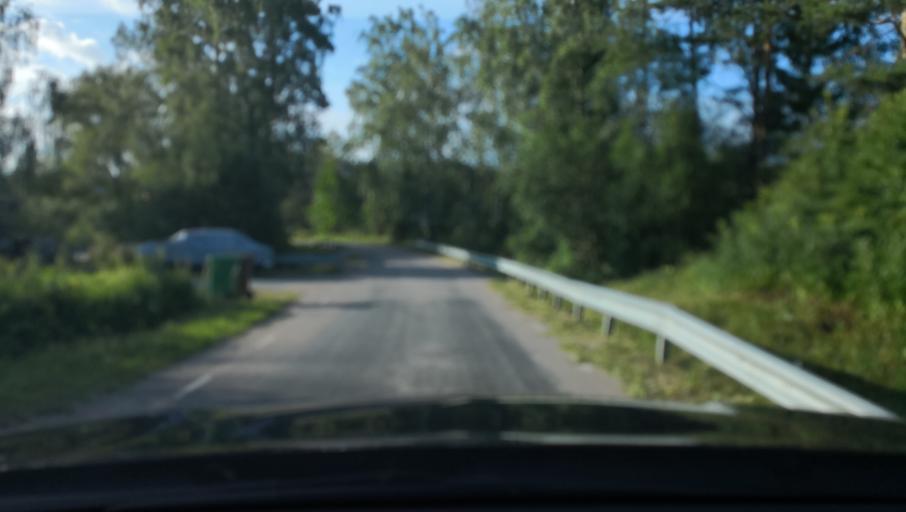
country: SE
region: Uppsala
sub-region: Osthammars Kommun
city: Osterbybruk
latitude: 60.0194
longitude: 17.9235
